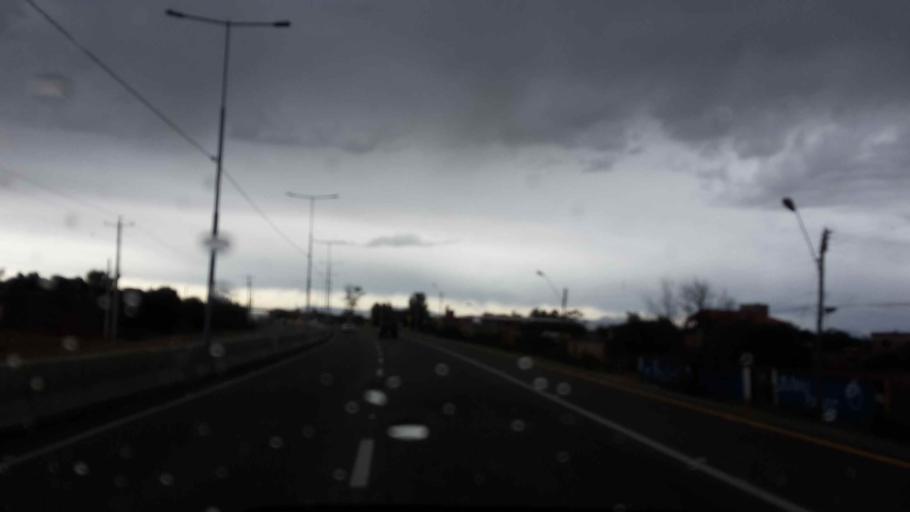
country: BO
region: Cochabamba
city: Tarata
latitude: -17.5400
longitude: -66.0654
